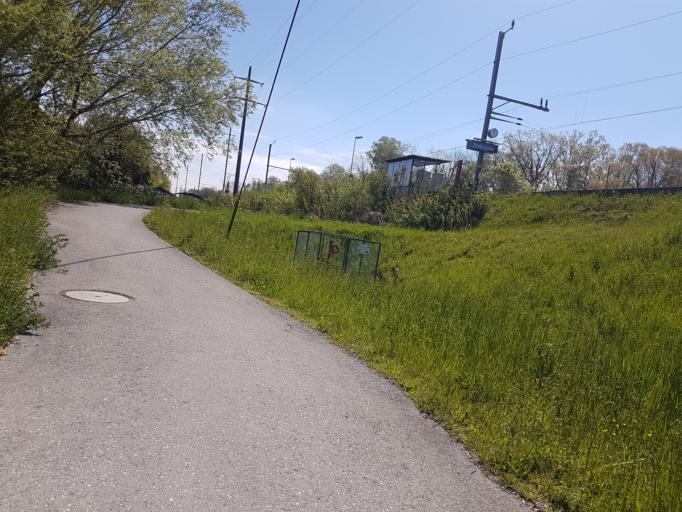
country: CH
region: Neuchatel
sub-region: Neuchatel District
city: Cornaux
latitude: 47.0096
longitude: 7.0300
